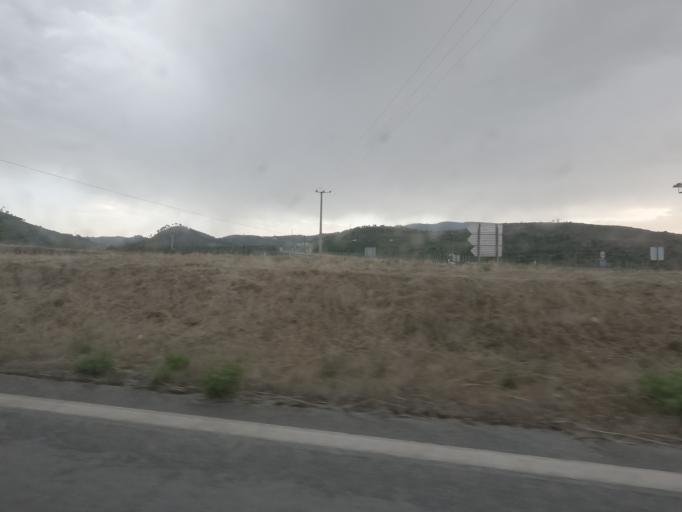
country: PT
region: Vila Real
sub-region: Peso da Regua
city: Peso da Regua
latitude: 41.1329
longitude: -7.7718
